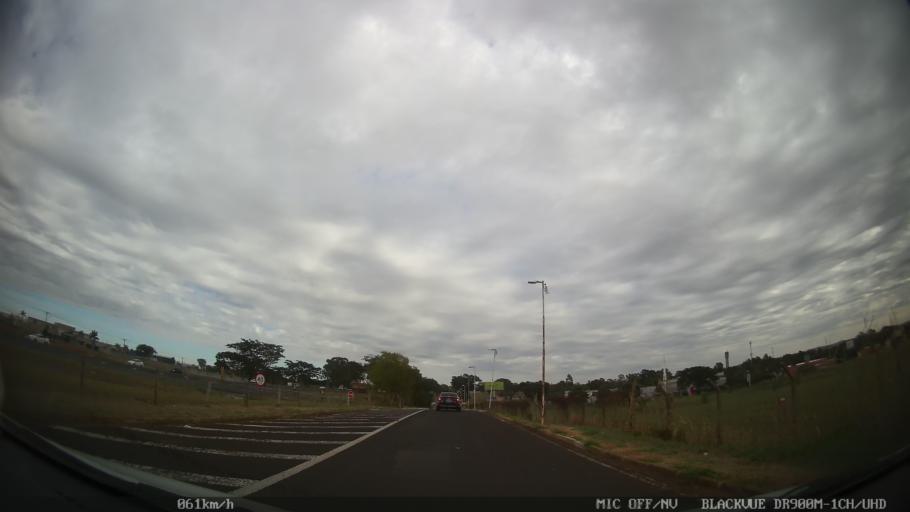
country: BR
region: Sao Paulo
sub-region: Sao Jose Do Rio Preto
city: Sao Jose do Rio Preto
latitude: -20.8231
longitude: -49.4160
